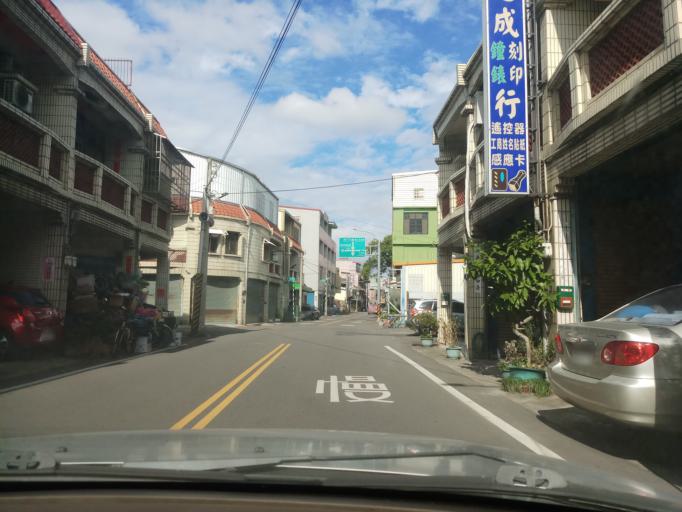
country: TW
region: Taiwan
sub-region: Miaoli
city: Miaoli
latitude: 24.6812
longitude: 120.8628
